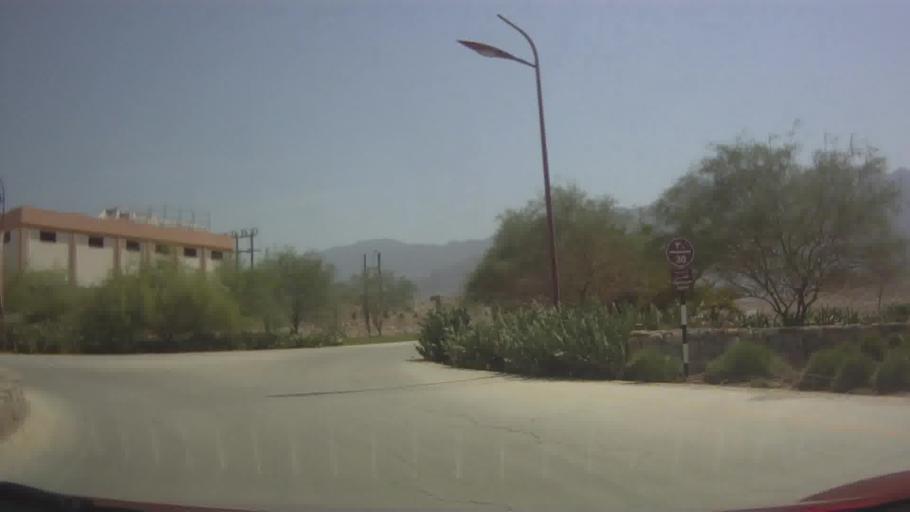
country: OM
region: Muhafazat Masqat
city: Muscat
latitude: 23.4134
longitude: 58.7849
